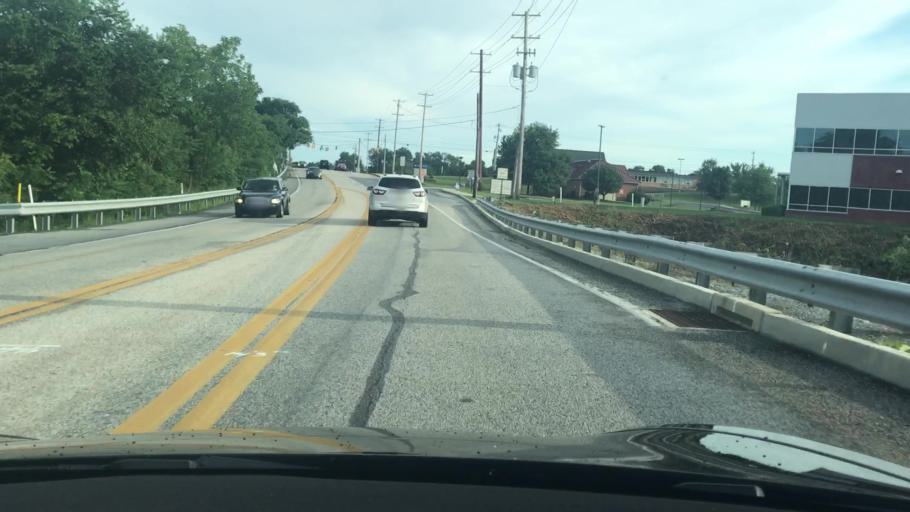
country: US
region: Pennsylvania
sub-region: Dauphin County
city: Colonial Park
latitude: 40.3082
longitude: -76.8240
